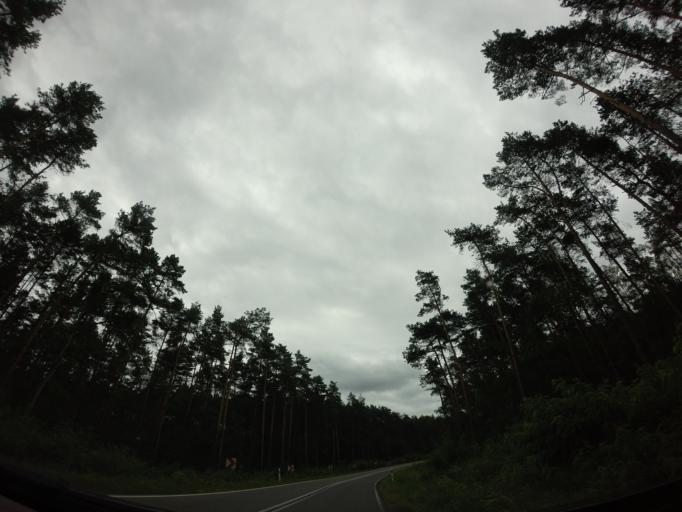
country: PL
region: Masovian Voivodeship
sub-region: Powiat makowski
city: Sypniewo
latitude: 53.0444
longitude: 21.3432
